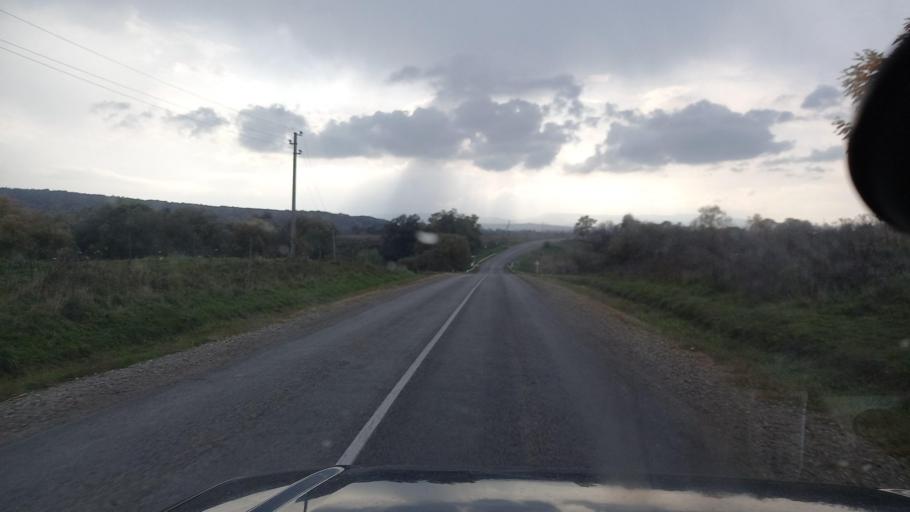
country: RU
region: Krasnodarskiy
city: Gubskaya
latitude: 44.3522
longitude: 40.6978
